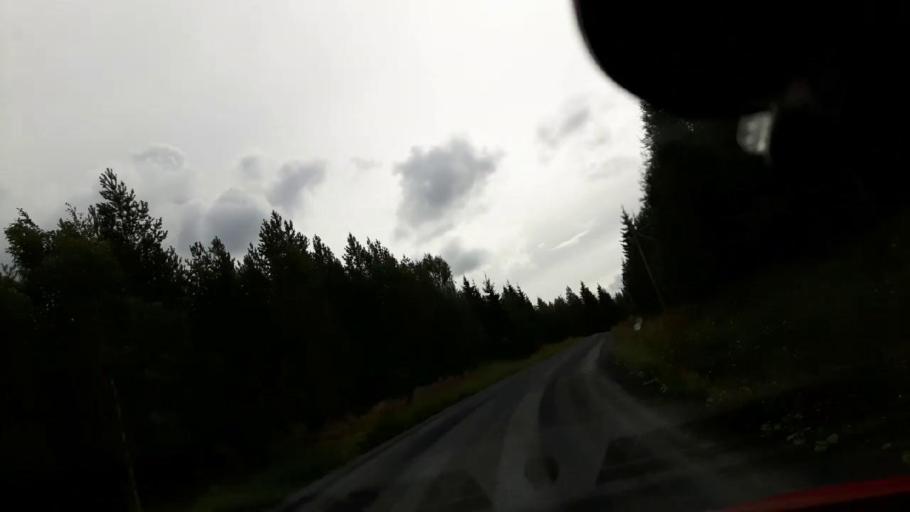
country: SE
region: Jaemtland
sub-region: Krokoms Kommun
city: Valla
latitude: 63.3808
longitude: 13.8865
